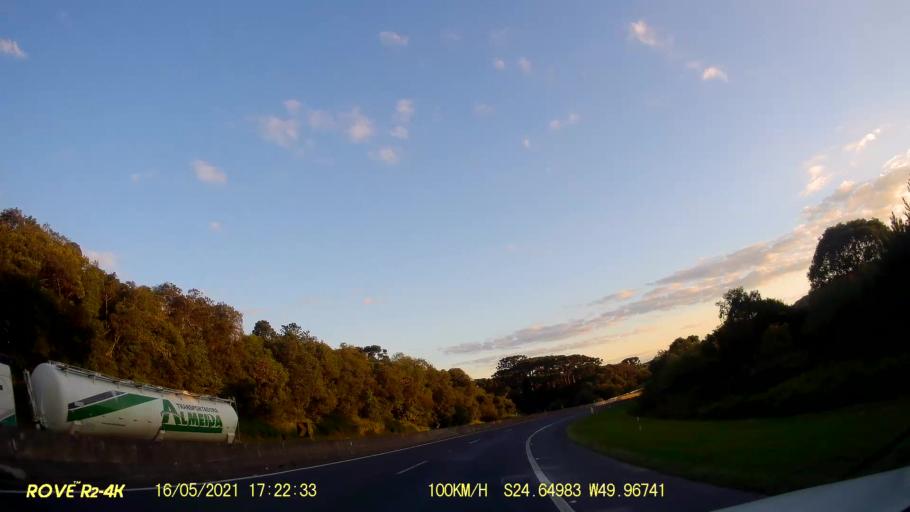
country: BR
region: Parana
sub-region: Pirai Do Sul
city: Pirai do Sul
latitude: -24.6502
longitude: -49.9673
